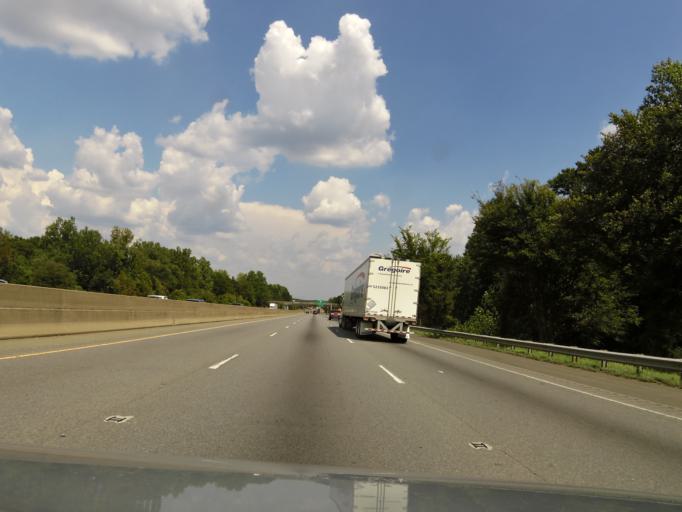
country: US
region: North Carolina
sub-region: Gaston County
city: Gastonia
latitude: 35.2821
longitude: -81.2132
